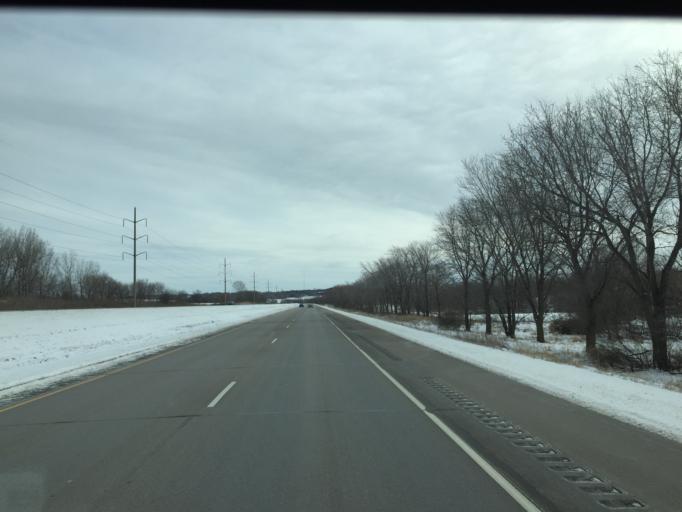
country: US
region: Minnesota
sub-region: Olmsted County
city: Byron
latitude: 44.0281
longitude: -92.5864
